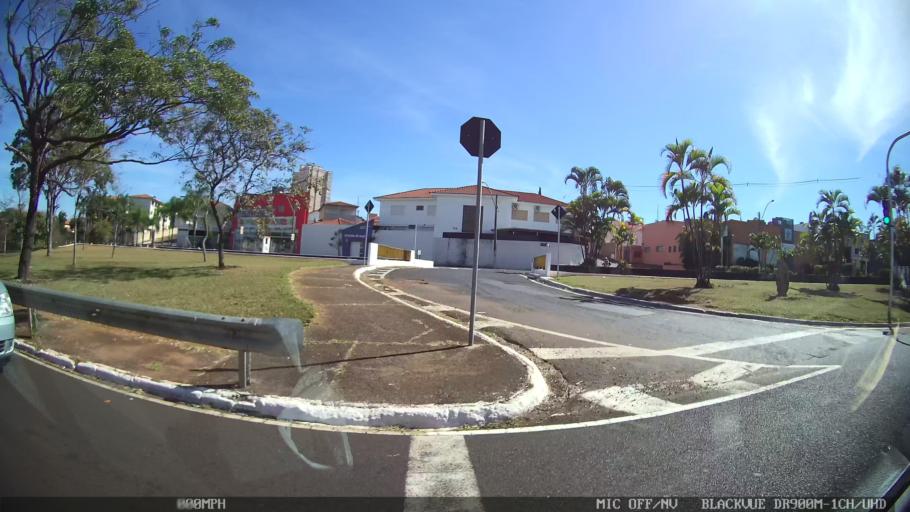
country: BR
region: Sao Paulo
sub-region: Franca
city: Franca
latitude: -20.5481
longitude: -47.4013
